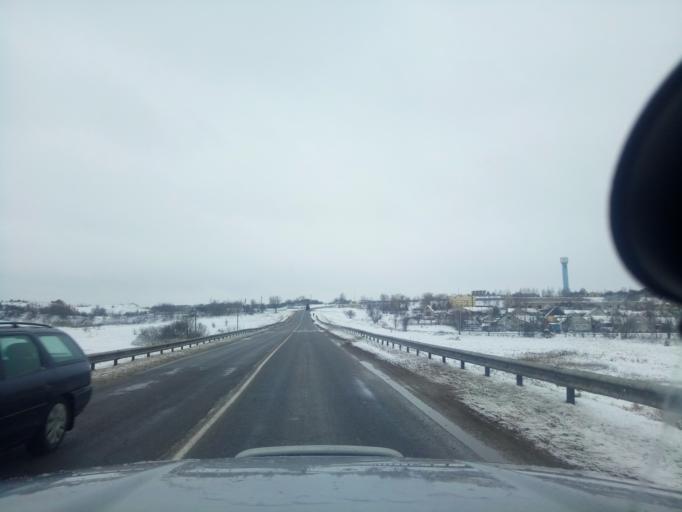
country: BY
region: Minsk
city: Kapyl'
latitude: 53.1438
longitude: 27.0794
